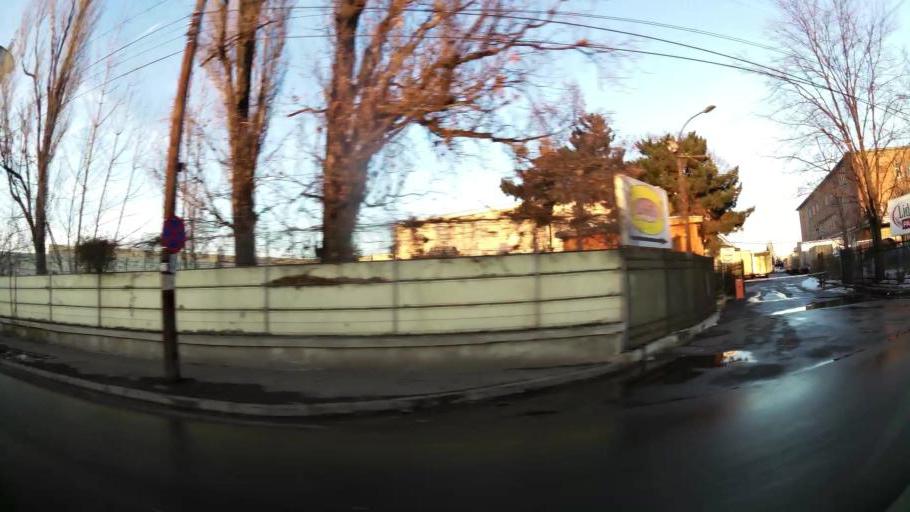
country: RO
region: Ilfov
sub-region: Comuna Fundeni-Dobroesti
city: Fundeni
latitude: 44.4517
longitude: 26.1366
